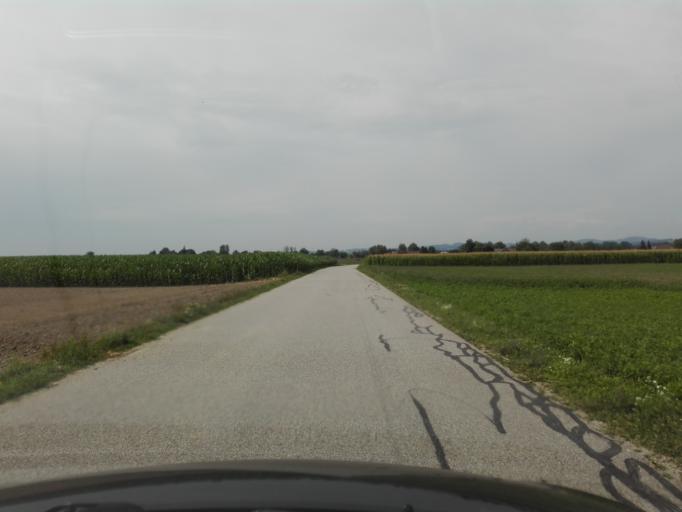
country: AT
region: Lower Austria
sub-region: Politischer Bezirk Amstetten
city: Strengberg
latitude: 48.1808
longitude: 14.6994
